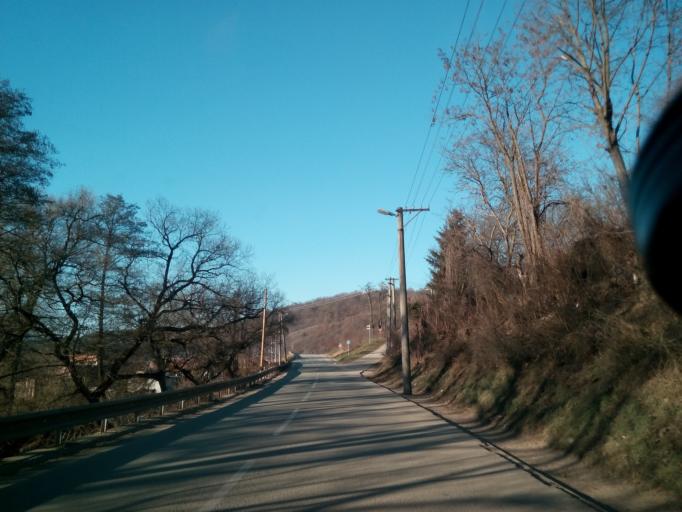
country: SK
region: Kosicky
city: Moldava nad Bodvou
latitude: 48.6843
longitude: 20.9723
